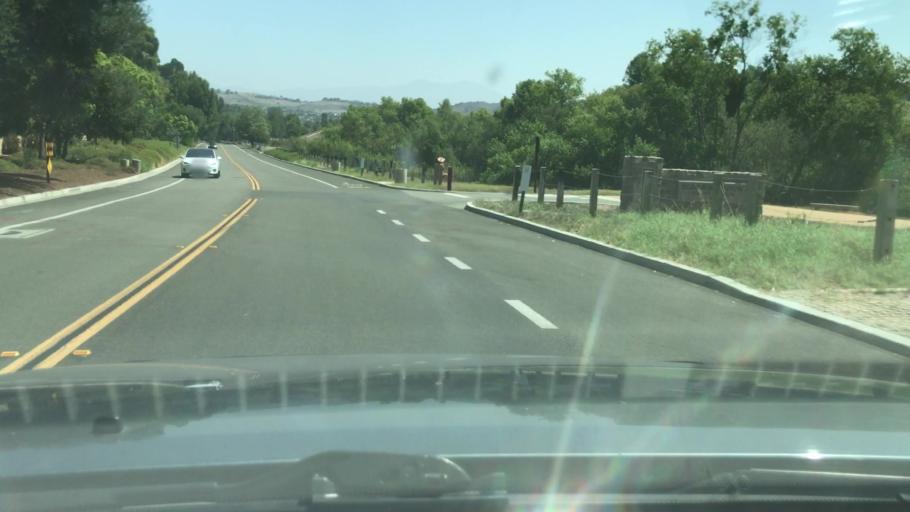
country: US
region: California
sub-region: Orange County
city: San Joaquin Hills
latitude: 33.6299
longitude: -117.8088
